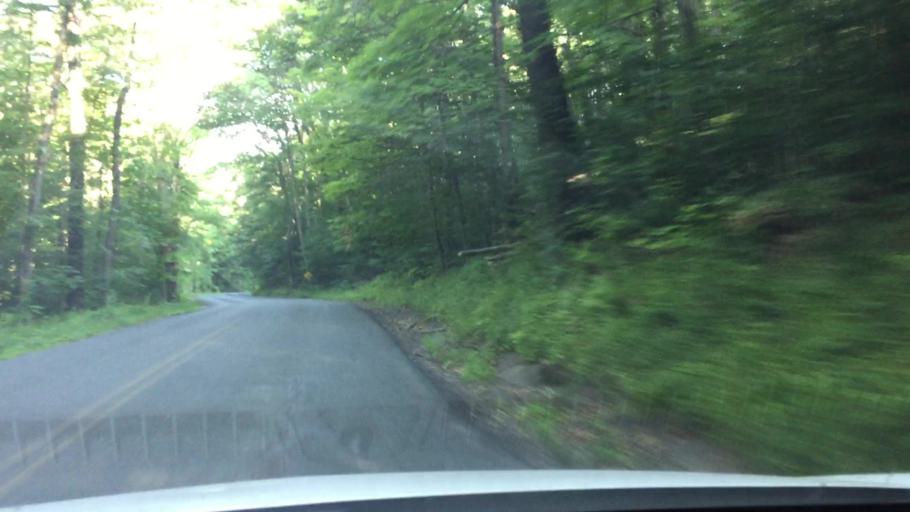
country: US
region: Massachusetts
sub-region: Berkshire County
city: Becket
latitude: 42.2966
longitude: -73.1494
